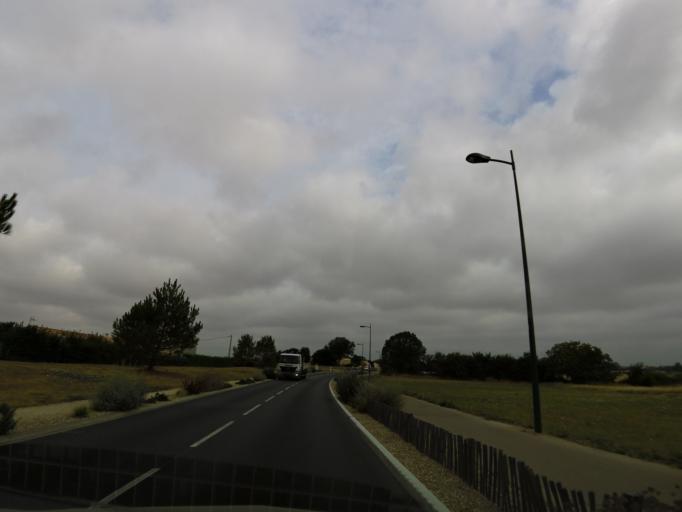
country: FR
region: Pays de la Loire
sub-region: Departement de la Vendee
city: Longeville-sur-Mer
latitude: 46.4124
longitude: -1.4944
